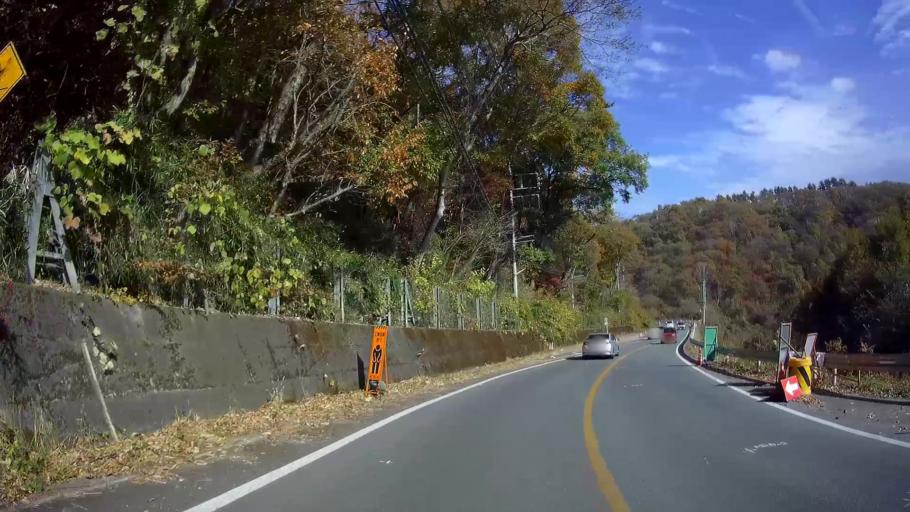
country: JP
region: Gunma
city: Nakanojomachi
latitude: 36.4950
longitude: 138.7753
